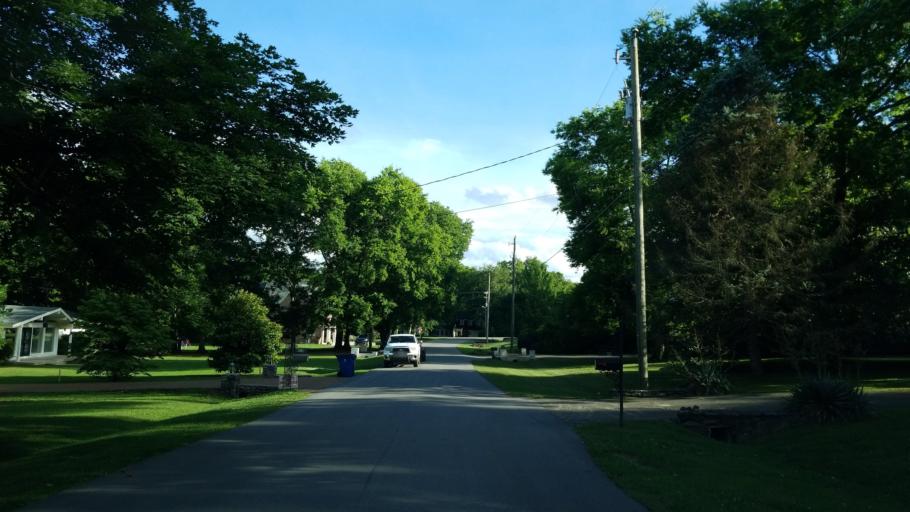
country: US
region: Tennessee
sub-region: Williamson County
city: Brentwood
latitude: 36.0276
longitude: -86.8044
